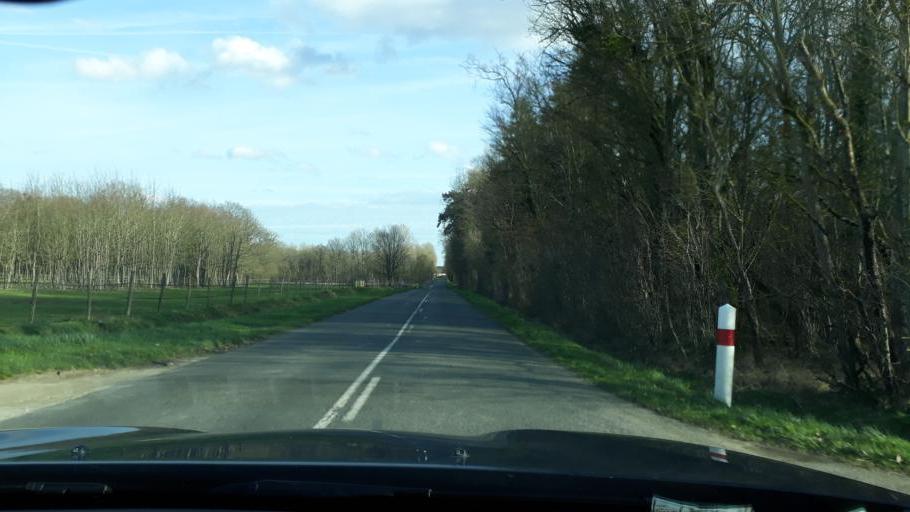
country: FR
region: Centre
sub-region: Departement du Loiret
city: Chilleurs-aux-Bois
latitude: 48.0628
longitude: 2.1544
